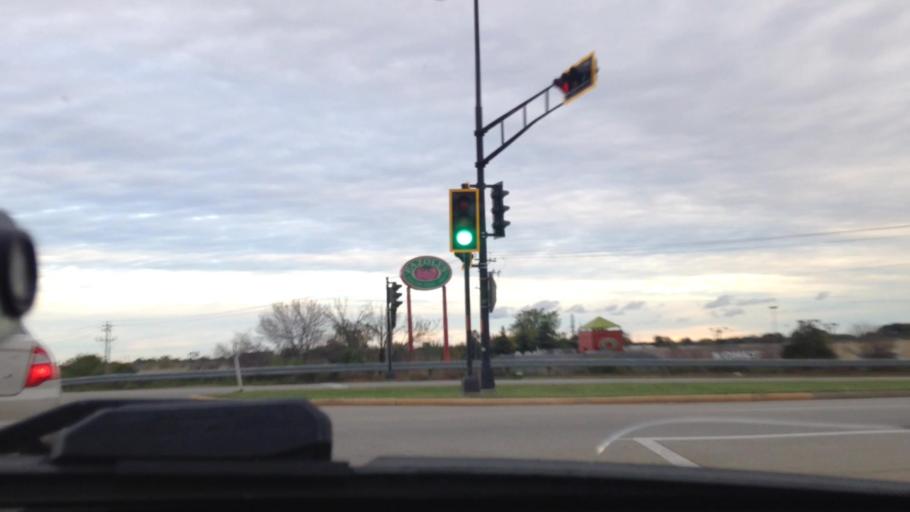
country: US
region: Wisconsin
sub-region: Fond du Lac County
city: North Fond du Lac
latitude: 43.7843
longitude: -88.4816
